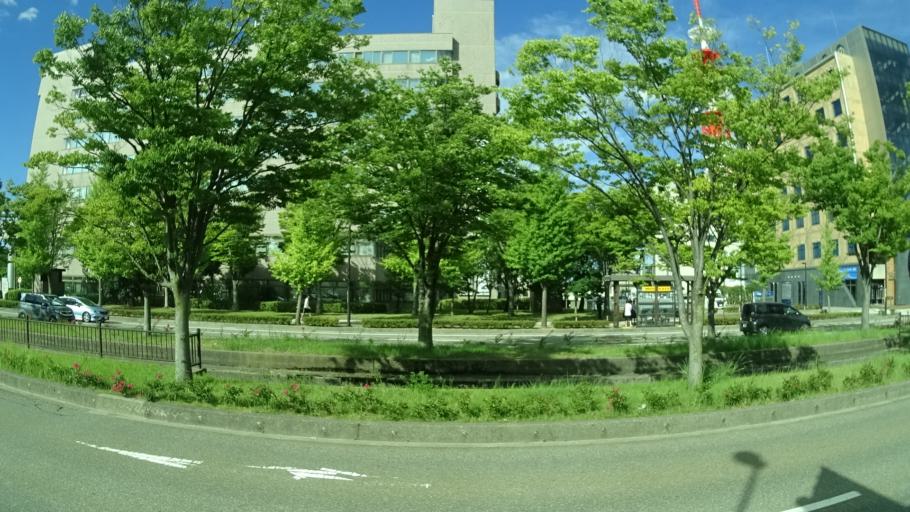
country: JP
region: Ishikawa
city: Kanazawa-shi
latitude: 36.5885
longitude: 136.6339
